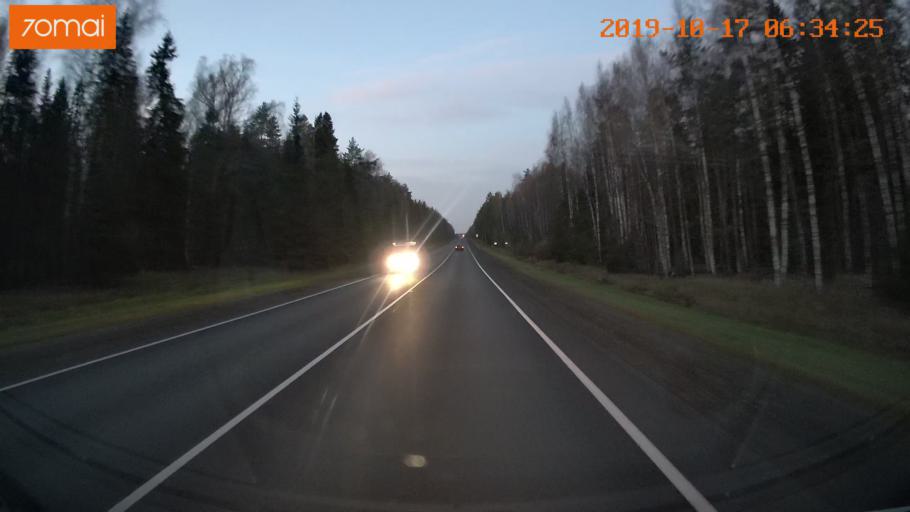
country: RU
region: Ivanovo
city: Novoye Leushino
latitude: 56.7034
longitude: 40.6389
